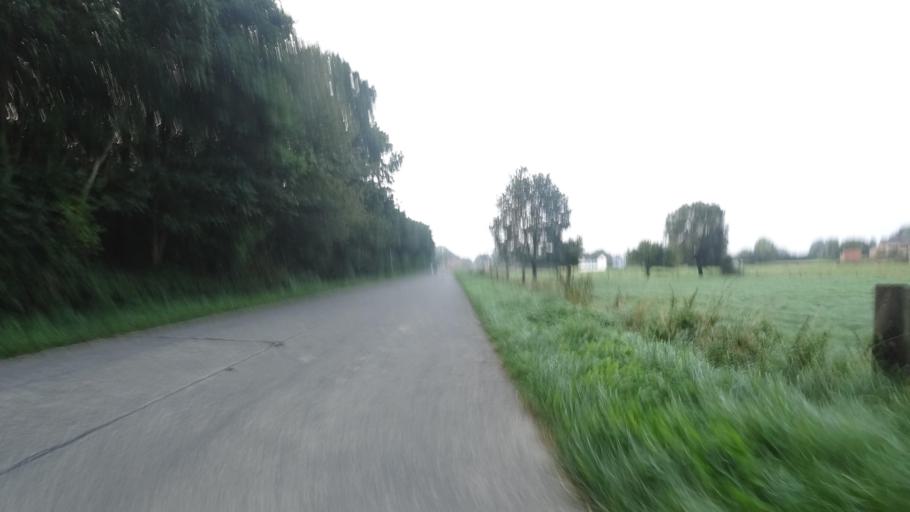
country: BE
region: Wallonia
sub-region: Province du Brabant Wallon
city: Perwez
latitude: 50.5953
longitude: 4.7785
